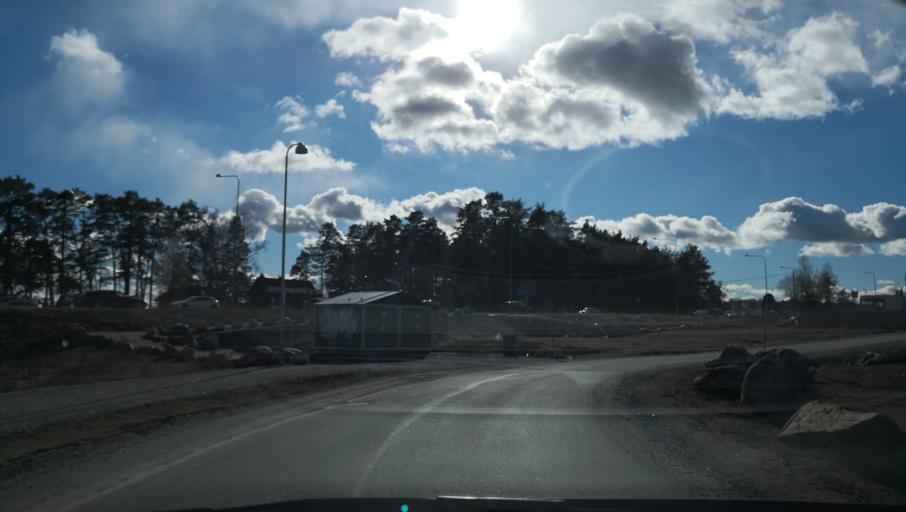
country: SE
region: Stockholm
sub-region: Varmdo Kommun
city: Mortnas
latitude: 59.3137
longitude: 18.4566
